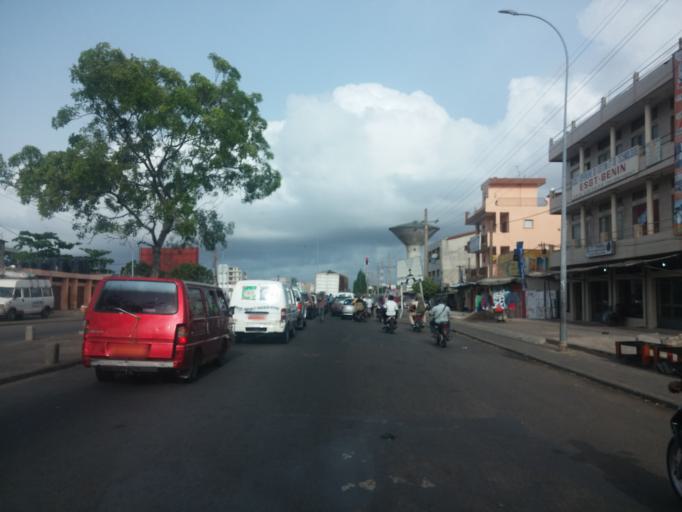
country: BJ
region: Littoral
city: Cotonou
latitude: 6.3770
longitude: 2.3910
